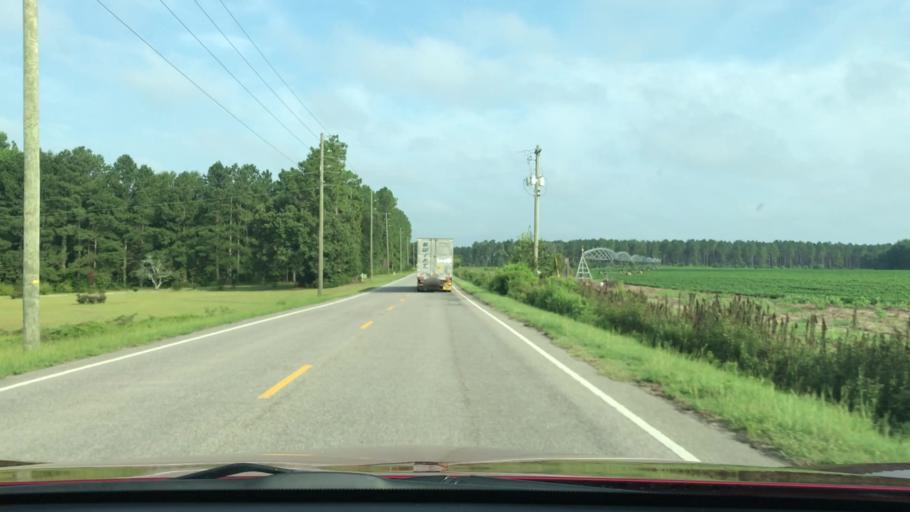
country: US
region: South Carolina
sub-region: Barnwell County
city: Williston
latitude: 33.6115
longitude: -81.2777
